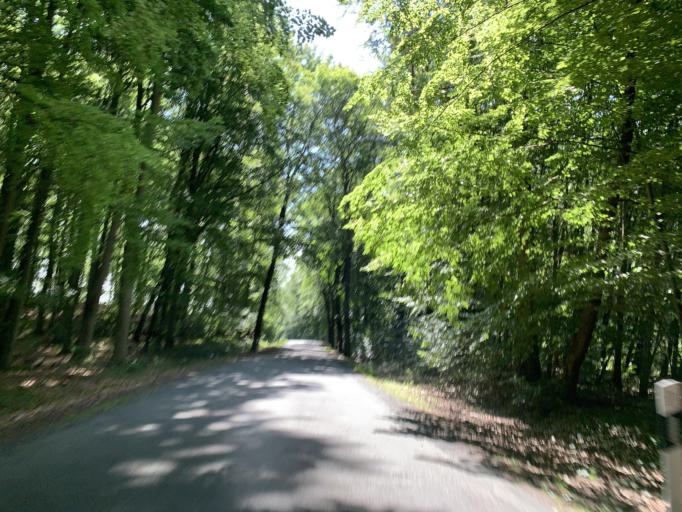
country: DE
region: Mecklenburg-Vorpommern
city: Carpin
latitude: 53.3315
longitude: 13.2424
